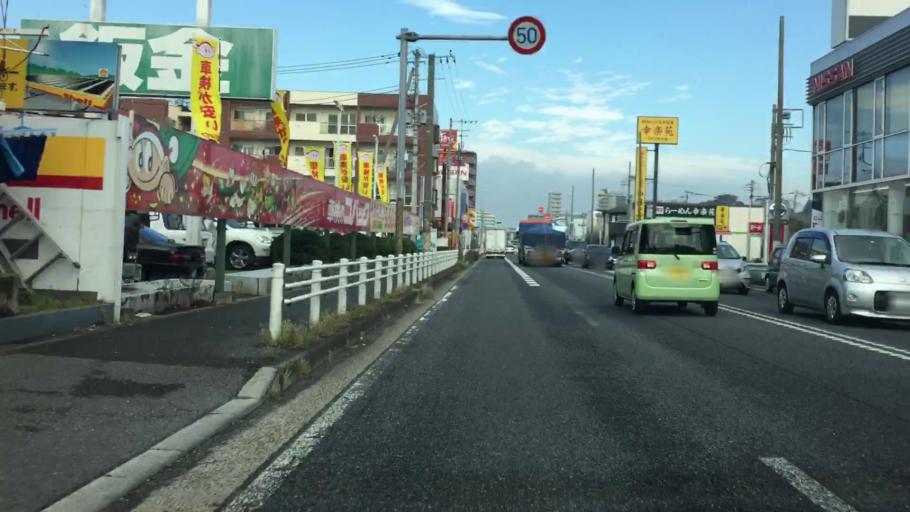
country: JP
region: Chiba
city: Matsudo
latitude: 35.7921
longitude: 139.9100
